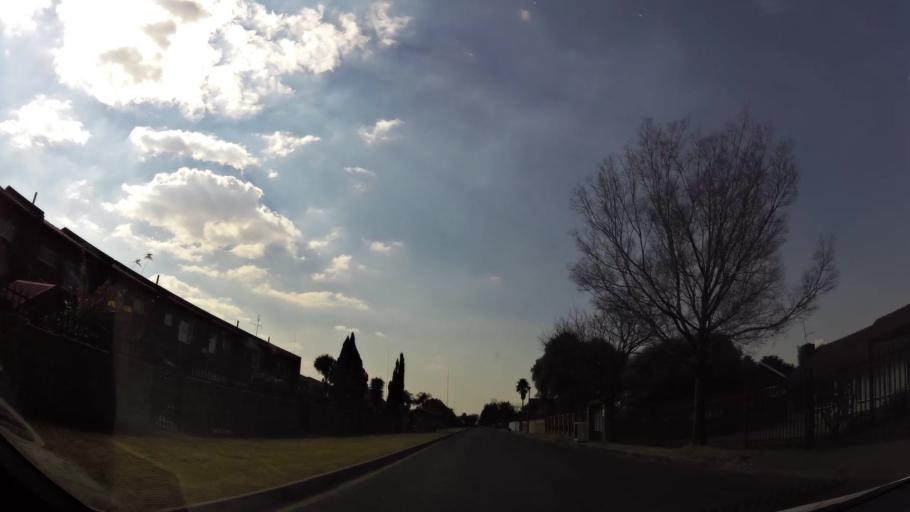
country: ZA
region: Gauteng
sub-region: Ekurhuleni Metropolitan Municipality
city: Boksburg
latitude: -26.1908
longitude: 28.2331
